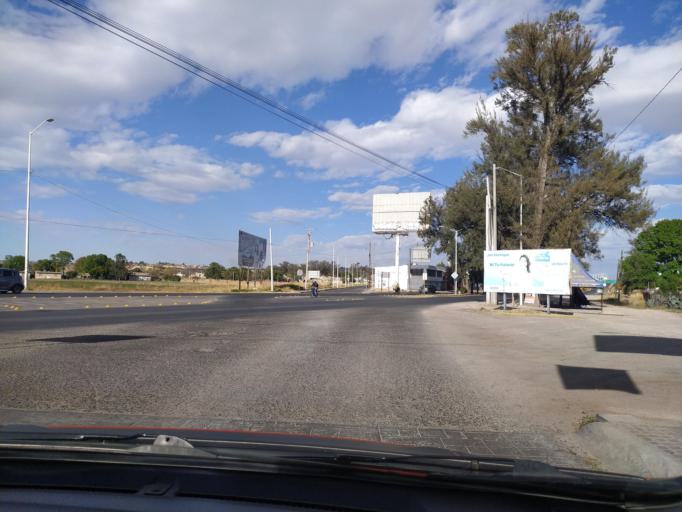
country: LA
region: Oudomxai
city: Muang La
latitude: 21.0323
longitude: 101.8291
